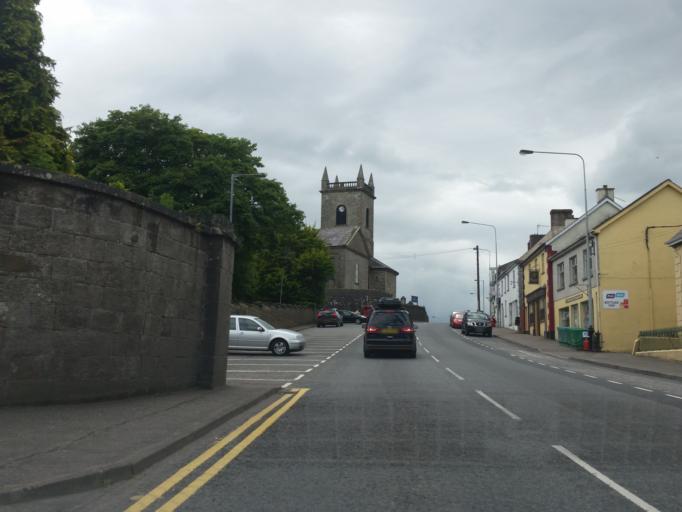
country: GB
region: Northern Ireland
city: Fivemiletown
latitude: 54.4112
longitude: -7.1712
